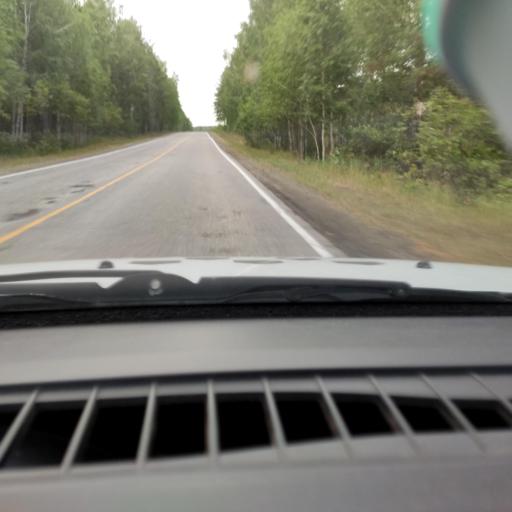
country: RU
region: Chelyabinsk
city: Ozersk
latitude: 55.8168
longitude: 60.6403
